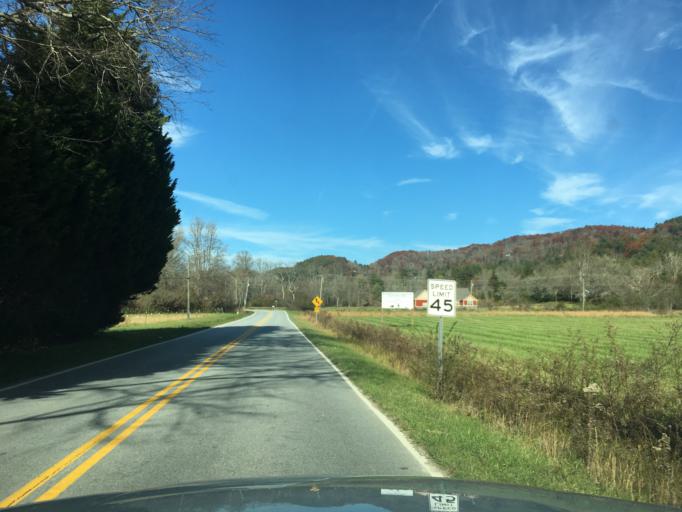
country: US
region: North Carolina
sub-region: Henderson County
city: Etowah
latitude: 35.2470
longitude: -82.6312
